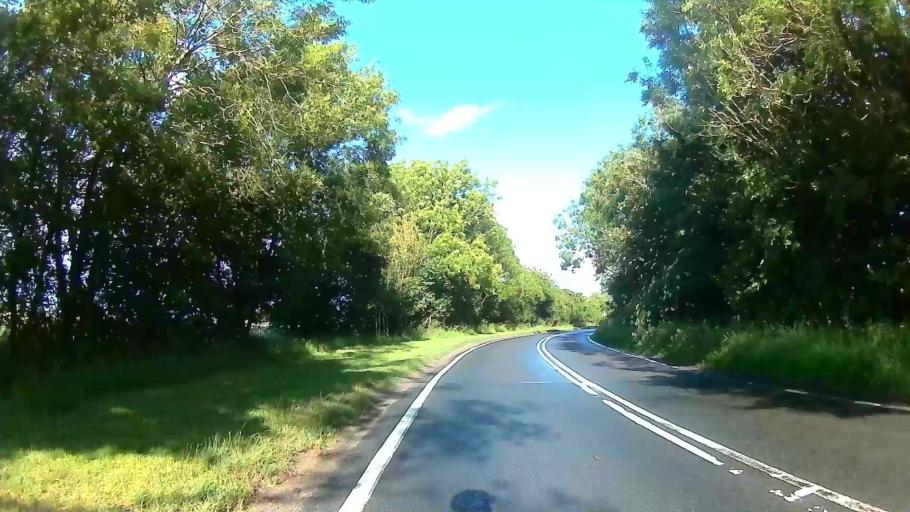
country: GB
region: England
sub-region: Essex
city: Ingatestone
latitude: 51.7147
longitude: 0.3806
